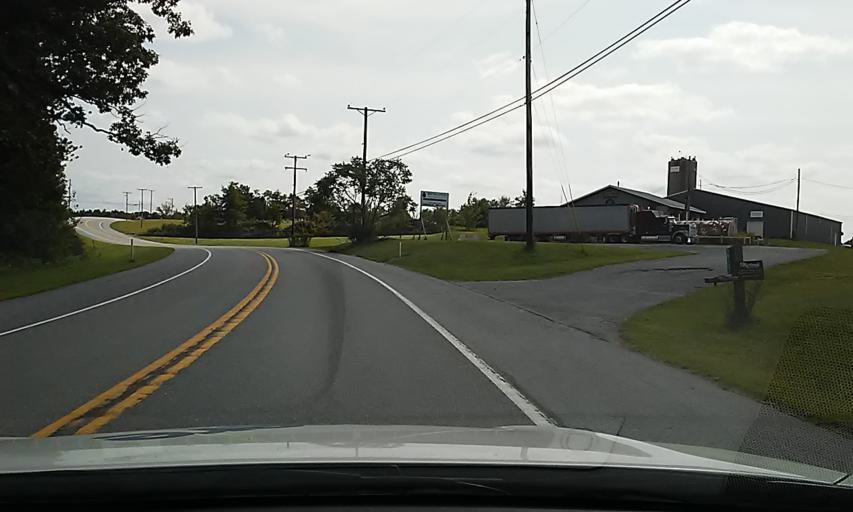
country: US
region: Pennsylvania
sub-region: Jefferson County
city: Punxsutawney
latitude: 40.8869
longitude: -79.0175
